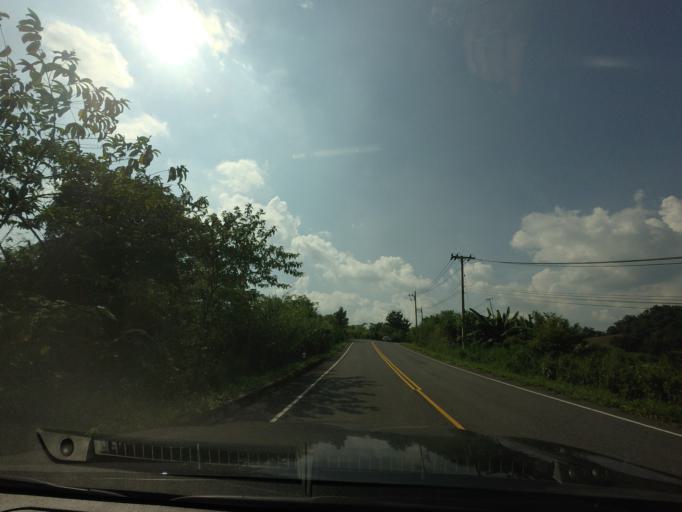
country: TH
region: Nan
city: Santi Suk
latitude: 18.9807
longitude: 101.0012
